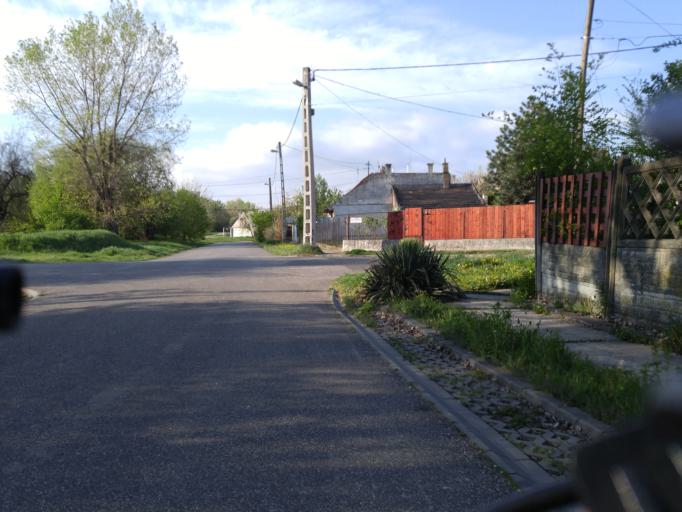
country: HU
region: Budapest
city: Budapest XIX. keruelet
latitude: 47.4307
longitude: 19.1329
